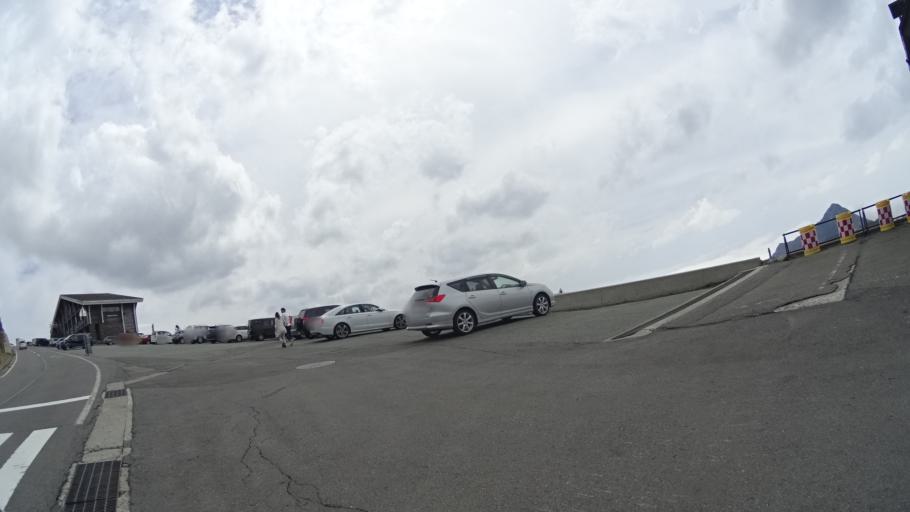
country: JP
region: Nagano
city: Nakano
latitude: 36.6700
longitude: 138.5187
